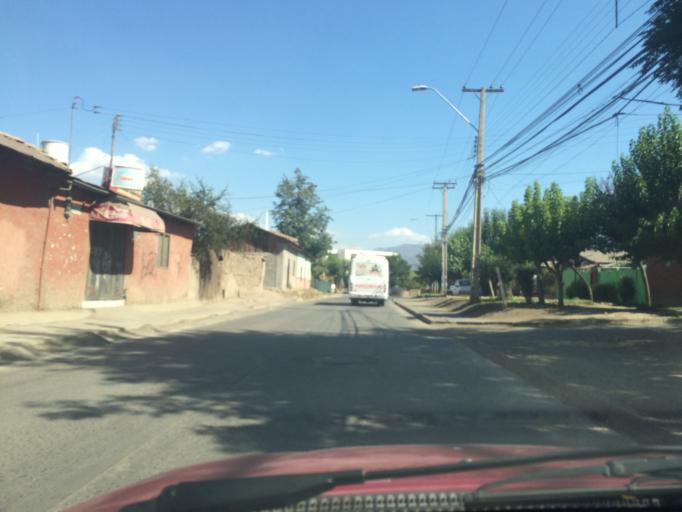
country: CL
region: Valparaiso
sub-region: Provincia de Los Andes
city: Los Andes
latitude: -32.8445
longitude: -70.5925
